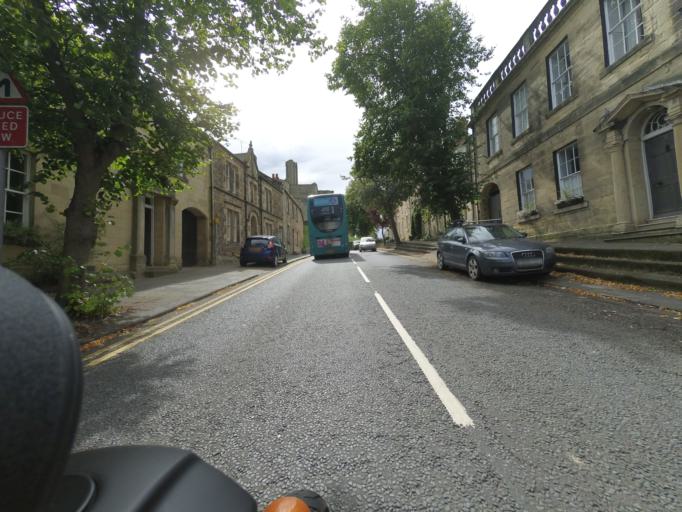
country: GB
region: England
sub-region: Northumberland
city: Warkworth
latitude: 55.3467
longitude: -1.6119
